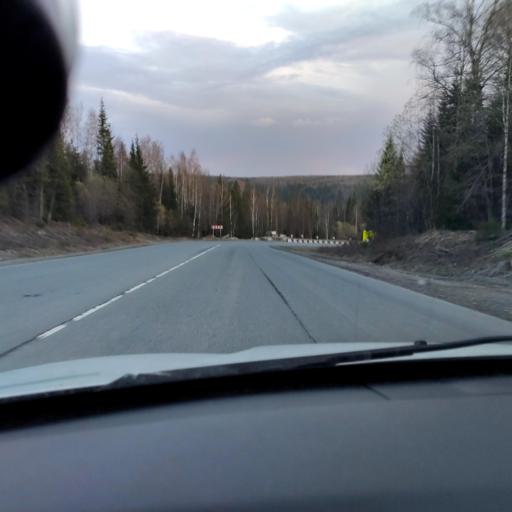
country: RU
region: Perm
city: Gremyachinsk
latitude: 58.4477
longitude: 57.8725
